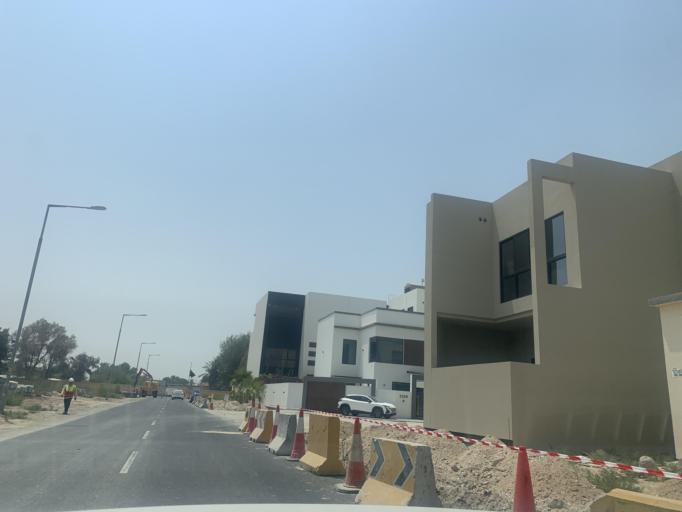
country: BH
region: Central Governorate
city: Madinat Hamad
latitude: 26.1470
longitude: 50.4667
